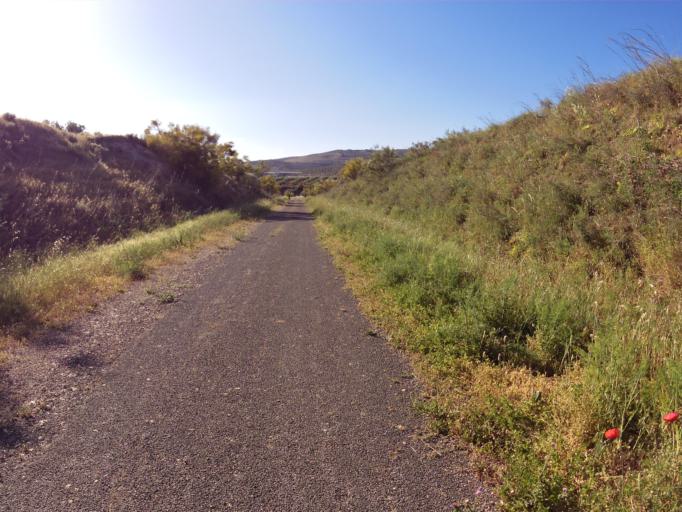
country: ES
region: Andalusia
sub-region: Province of Cordoba
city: Luque
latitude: 37.5662
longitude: -4.2469
